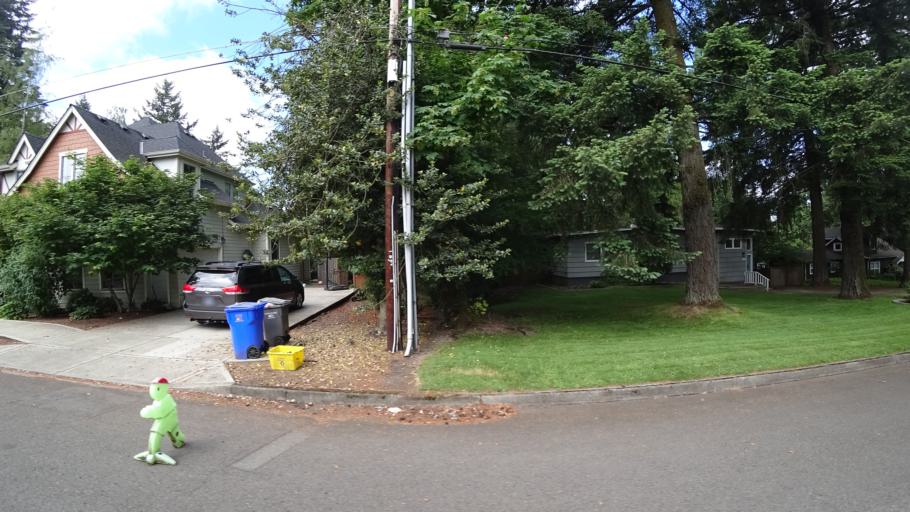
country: US
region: Oregon
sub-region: Washington County
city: Metzger
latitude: 45.4535
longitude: -122.7300
